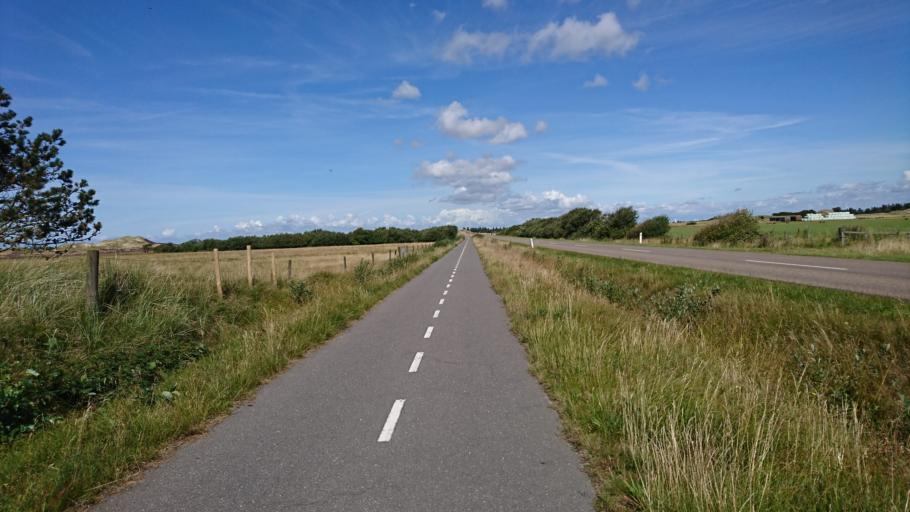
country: DK
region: South Denmark
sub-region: Fano Kommune
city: Nordby
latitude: 55.3631
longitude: 8.4575
